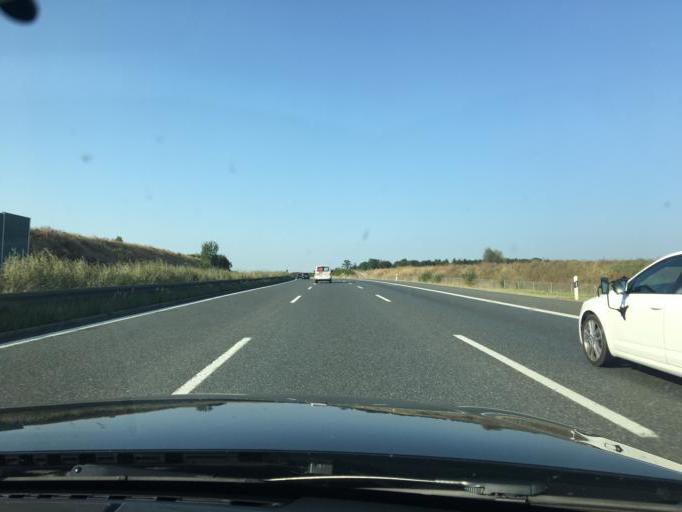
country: DE
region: Bavaria
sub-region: Upper Bavaria
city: Stammham
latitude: 48.8719
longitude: 11.4679
